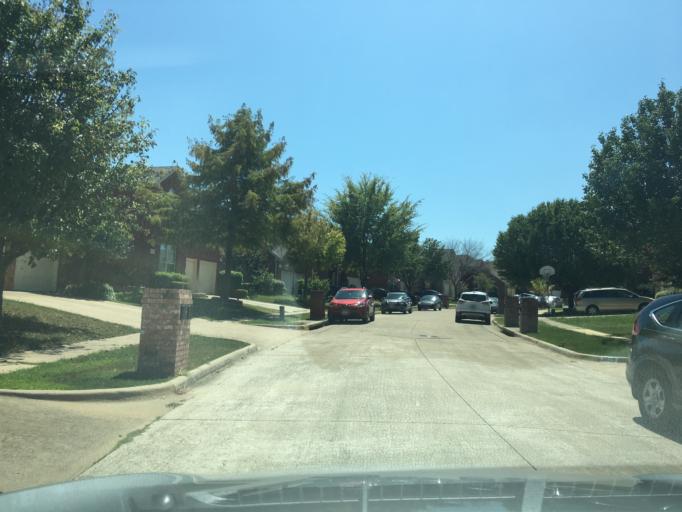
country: US
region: Texas
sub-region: Dallas County
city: Garland
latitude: 32.9529
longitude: -96.6435
